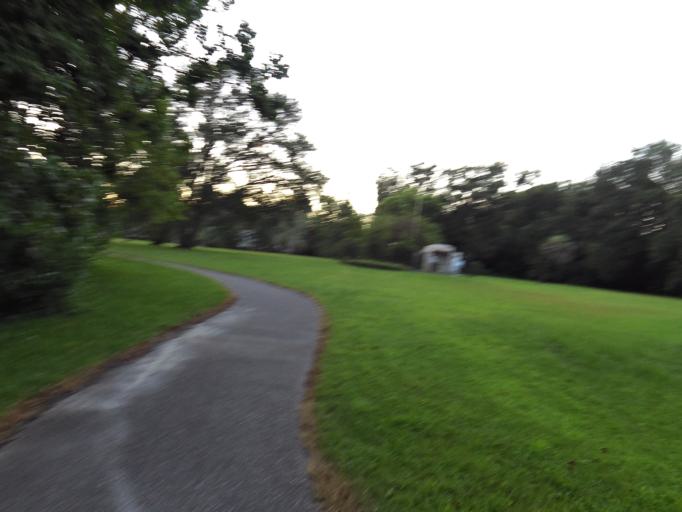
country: US
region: Florida
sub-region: Duval County
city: Jacksonville
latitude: 30.3016
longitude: -81.6469
